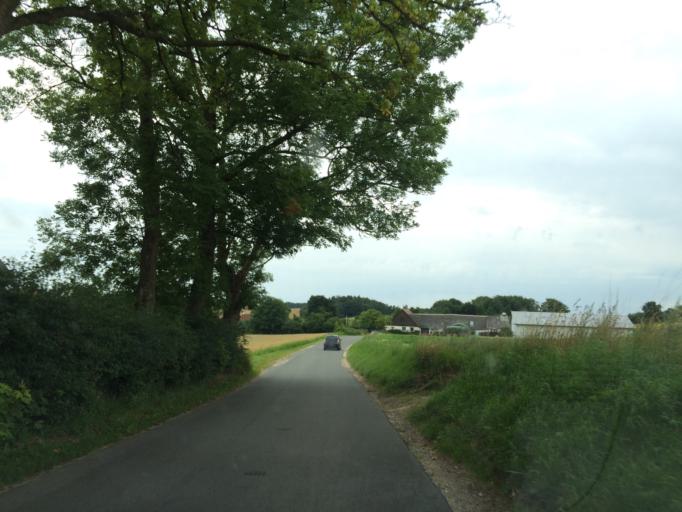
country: DK
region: Central Jutland
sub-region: Syddjurs Kommune
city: Ronde
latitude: 56.2352
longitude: 10.5245
